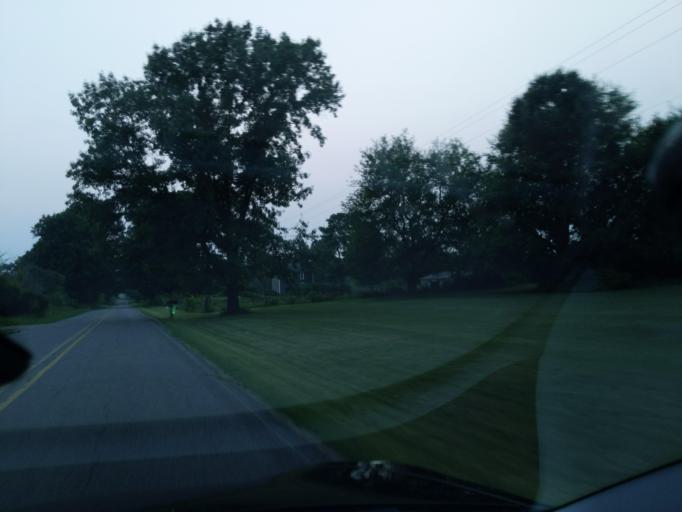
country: US
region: Michigan
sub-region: Ingham County
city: Leslie
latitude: 42.3715
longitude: -84.4968
